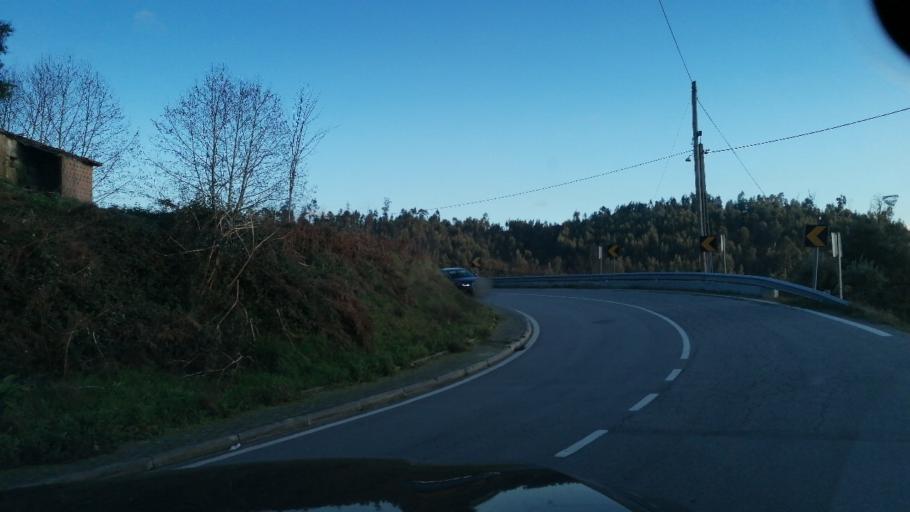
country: PT
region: Vila Real
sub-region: Mondim de Basto
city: Mondim de Basto
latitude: 41.4333
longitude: -7.9795
